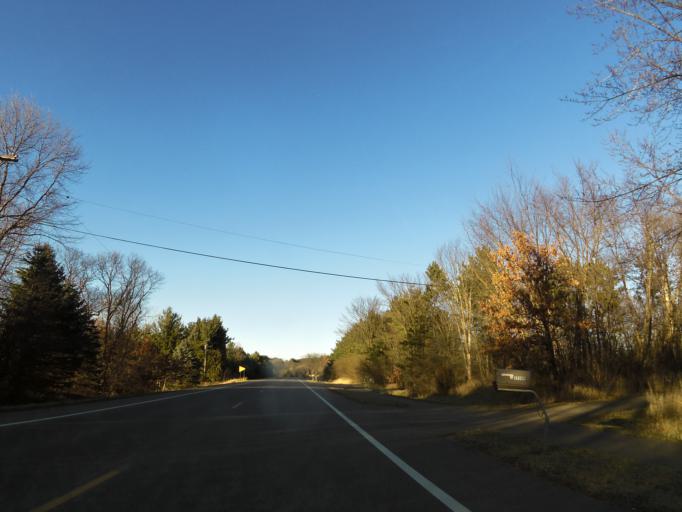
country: US
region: Minnesota
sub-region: Washington County
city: Stillwater
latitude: 45.1111
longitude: -92.8333
